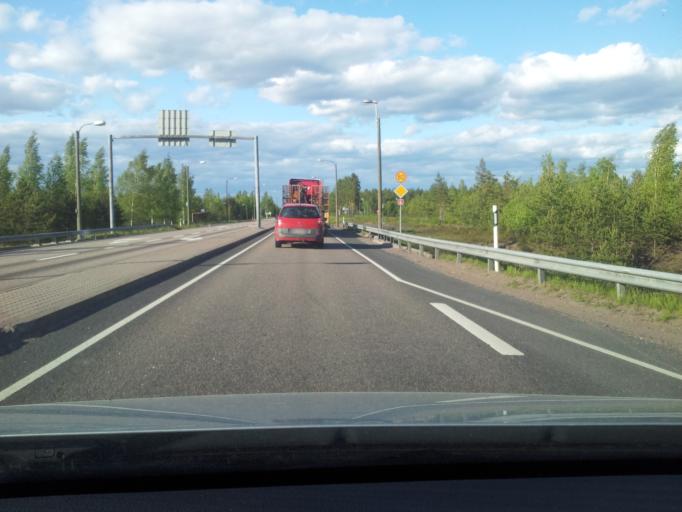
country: FI
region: Kymenlaakso
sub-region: Kouvola
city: Kouvola
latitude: 60.8954
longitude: 26.9115
